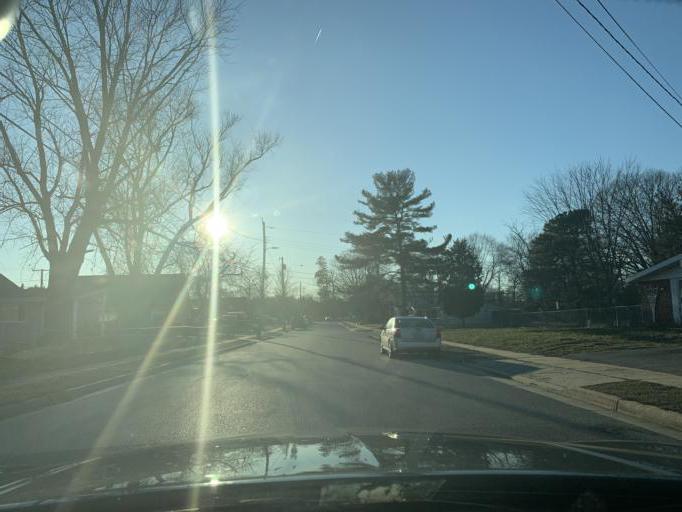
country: US
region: Maryland
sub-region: Anne Arundel County
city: South Gate
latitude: 39.1455
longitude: -76.6280
